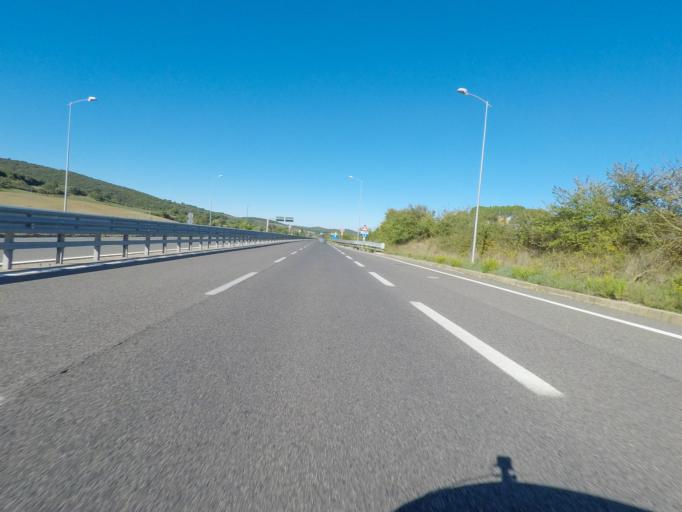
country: IT
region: Tuscany
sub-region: Provincia di Grosseto
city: Campagnatico
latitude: 42.8923
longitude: 11.2372
